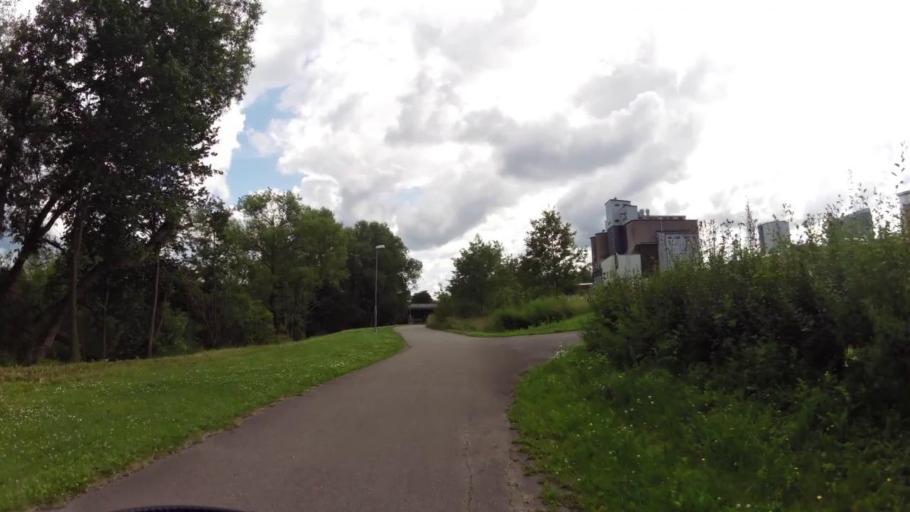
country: SE
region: OEstergoetland
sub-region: Linkopings Kommun
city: Linkoping
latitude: 58.4235
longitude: 15.6297
